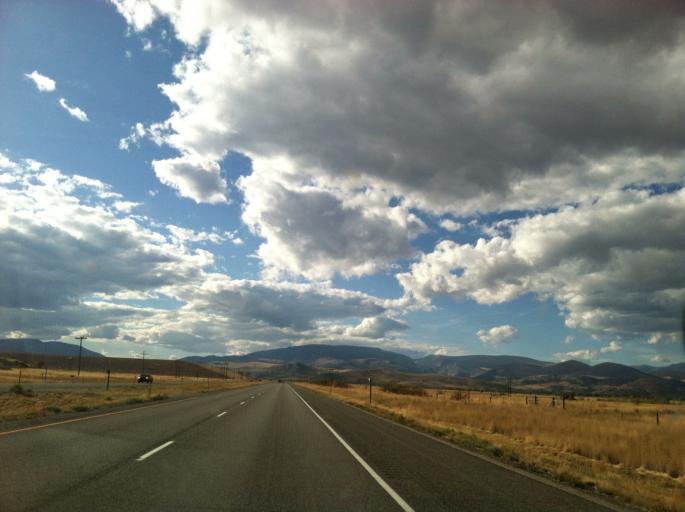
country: US
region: Montana
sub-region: Deer Lodge County
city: Anaconda
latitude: 46.1136
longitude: -112.8627
